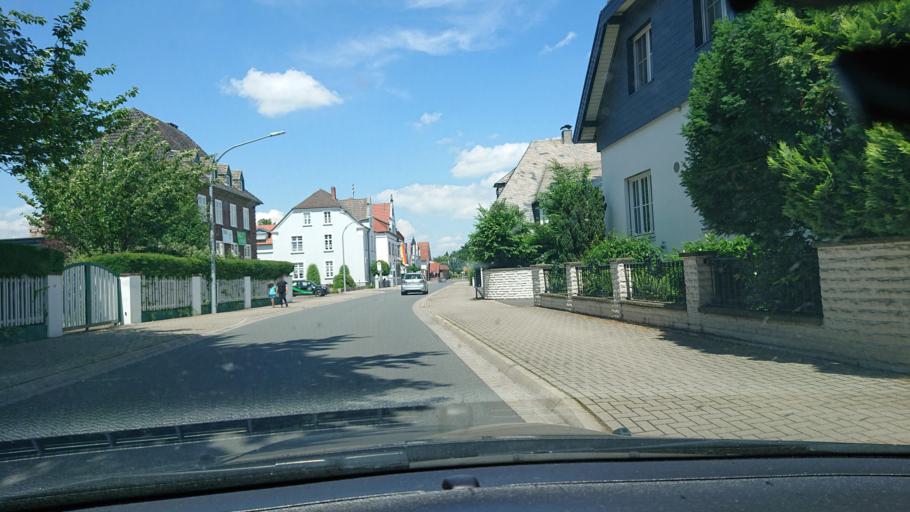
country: DE
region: North Rhine-Westphalia
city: Preussisch Oldendorf
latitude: 52.3046
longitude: 8.4911
